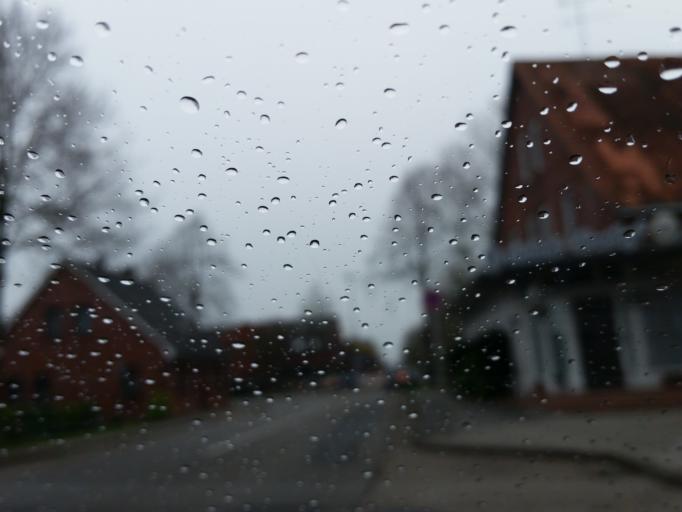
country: DE
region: Lower Saxony
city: Hollnseth
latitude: 53.5519
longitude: 9.1237
